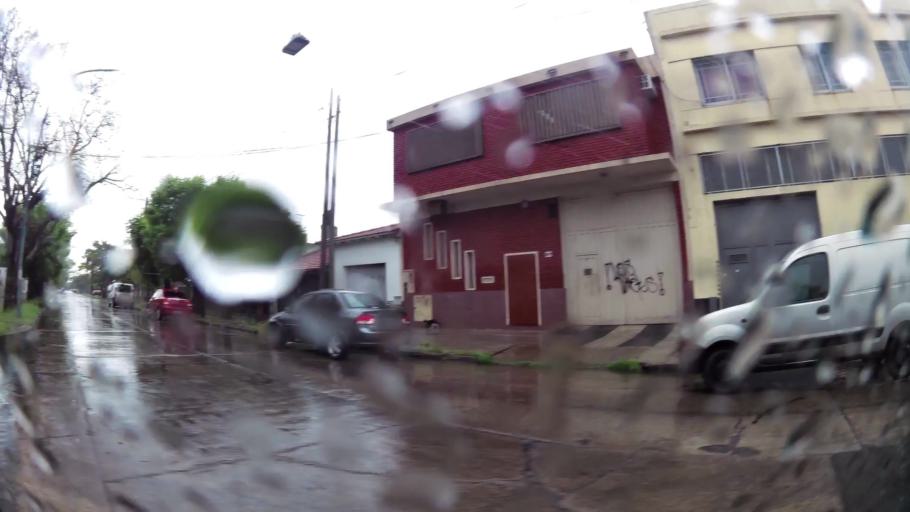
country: AR
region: Buenos Aires
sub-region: Partido de Lanus
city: Lanus
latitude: -34.7174
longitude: -58.4004
